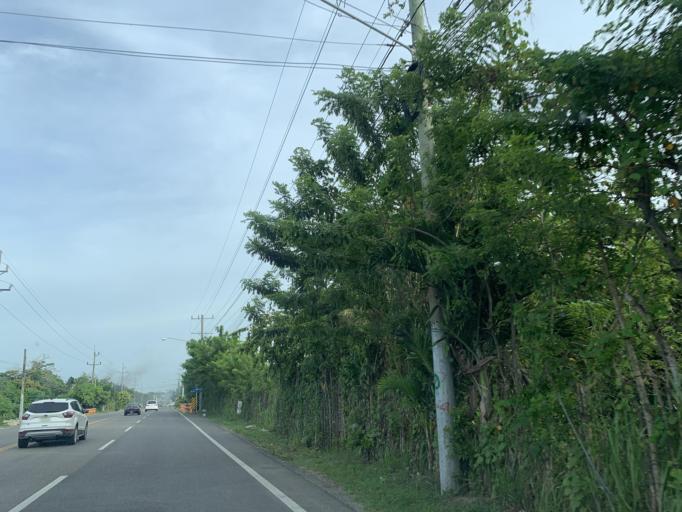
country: DO
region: Puerto Plata
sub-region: Puerto Plata
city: Puerto Plata
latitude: 19.7560
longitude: -70.6437
